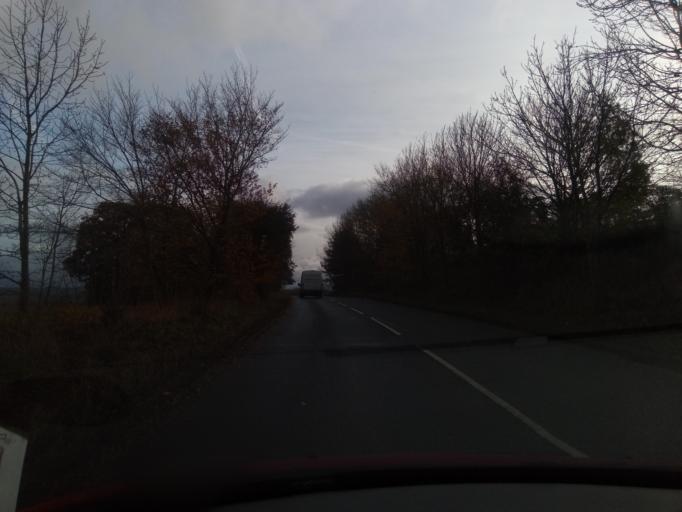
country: GB
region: England
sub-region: Northumberland
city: Birtley
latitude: 55.0459
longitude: -2.1535
